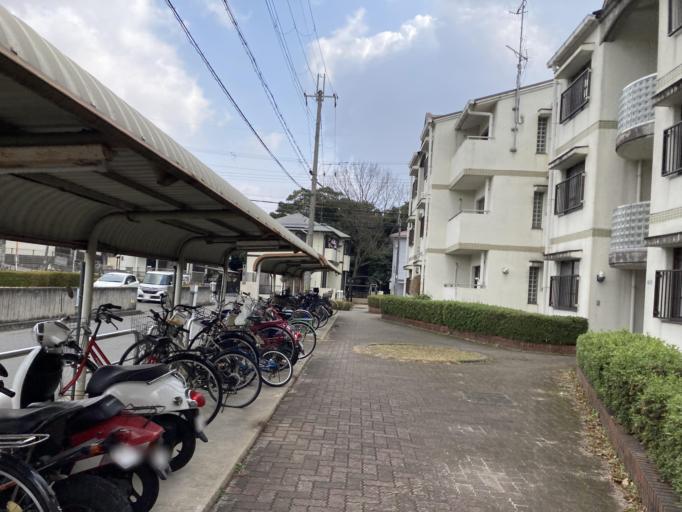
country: JP
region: Nara
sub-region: Ikoma-shi
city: Ikoma
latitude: 34.6088
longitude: 135.7241
